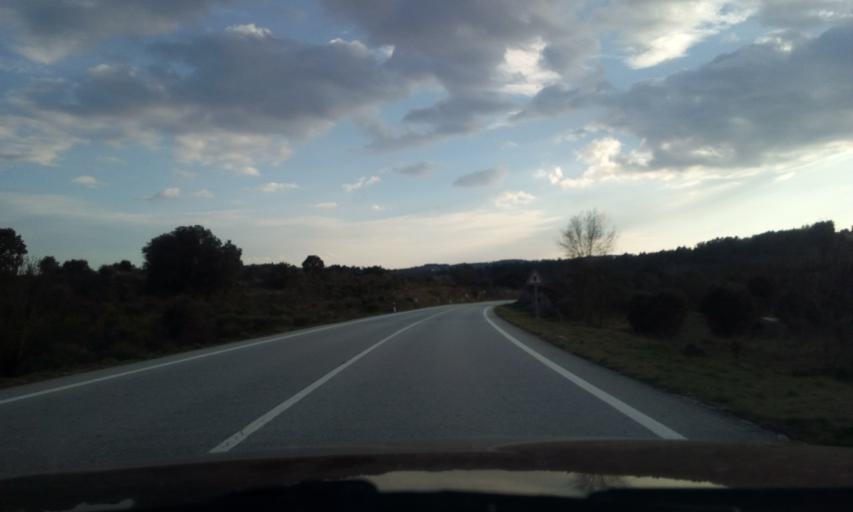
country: PT
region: Guarda
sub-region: Pinhel
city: Pinhel
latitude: 40.6749
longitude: -6.9504
